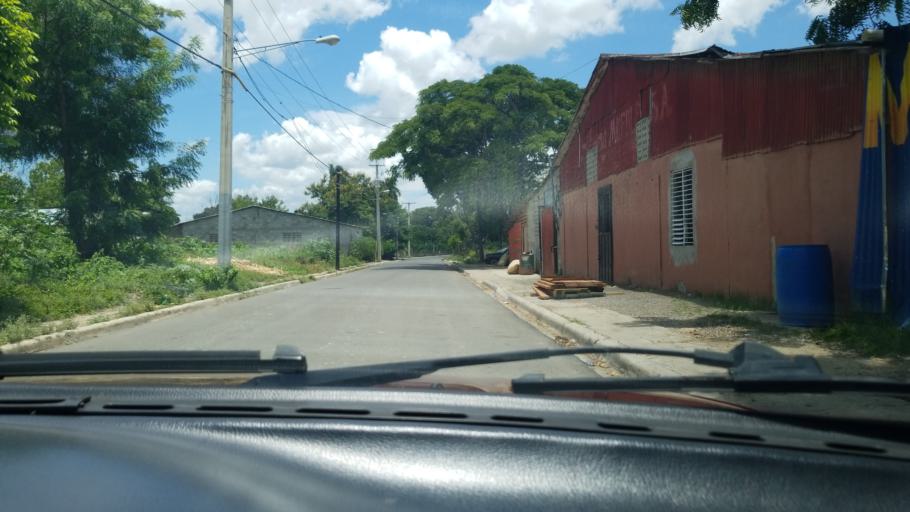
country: DO
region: Santiago
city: Santiago de los Caballeros
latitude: 19.5024
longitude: -70.6717
